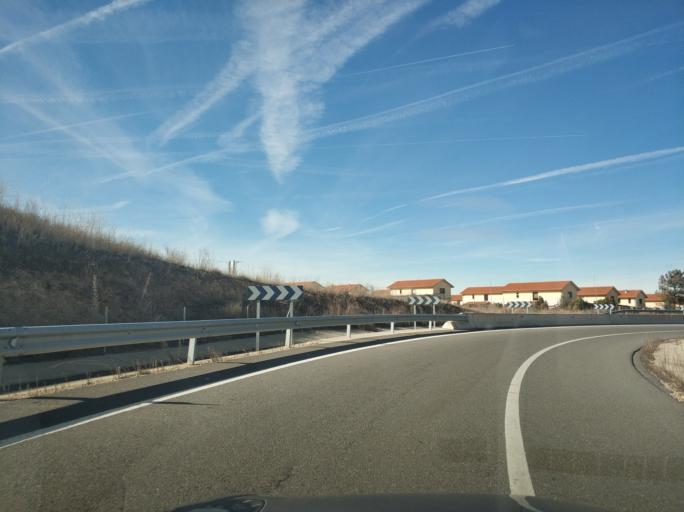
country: ES
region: Castille and Leon
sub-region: Provincia de Salamanca
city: Castellanos de Villiquera
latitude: 41.0308
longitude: -5.6748
